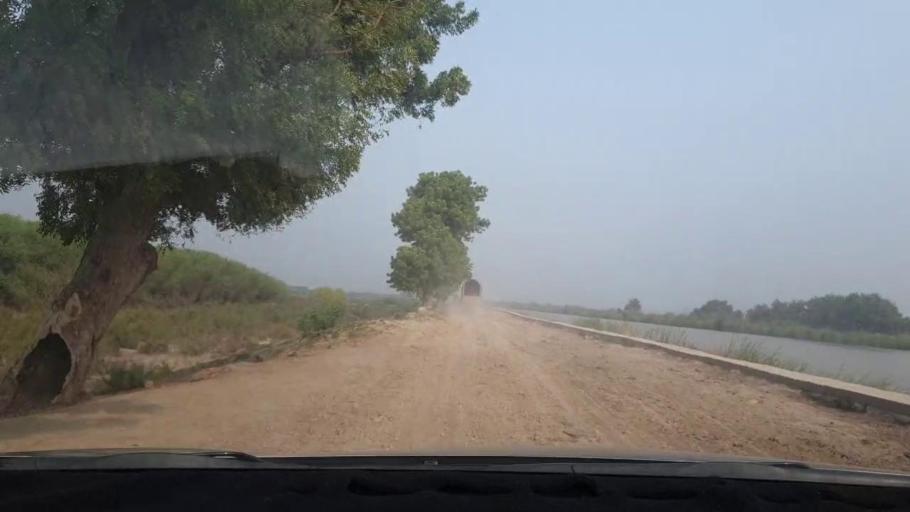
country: PK
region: Sindh
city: Matiari
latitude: 25.6521
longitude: 68.5614
